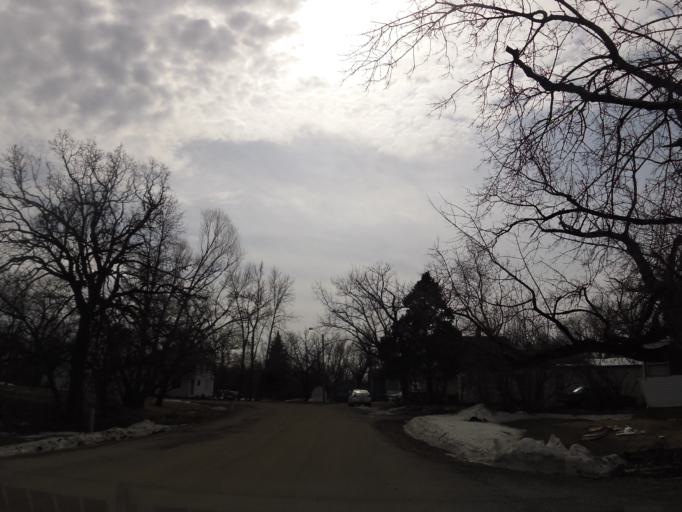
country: US
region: North Dakota
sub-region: Walsh County
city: Grafton
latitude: 48.2857
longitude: -97.3698
